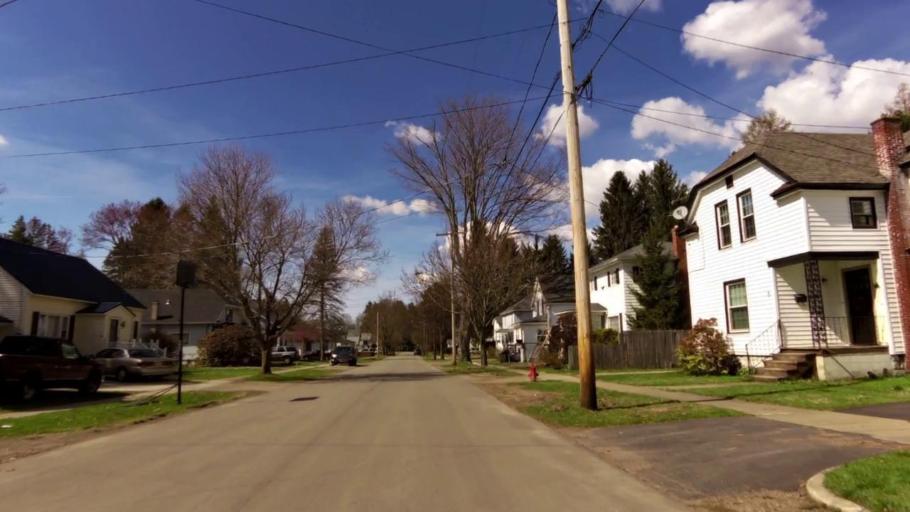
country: US
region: New York
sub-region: Cattaraugus County
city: Franklinville
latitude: 42.3378
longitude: -78.4508
